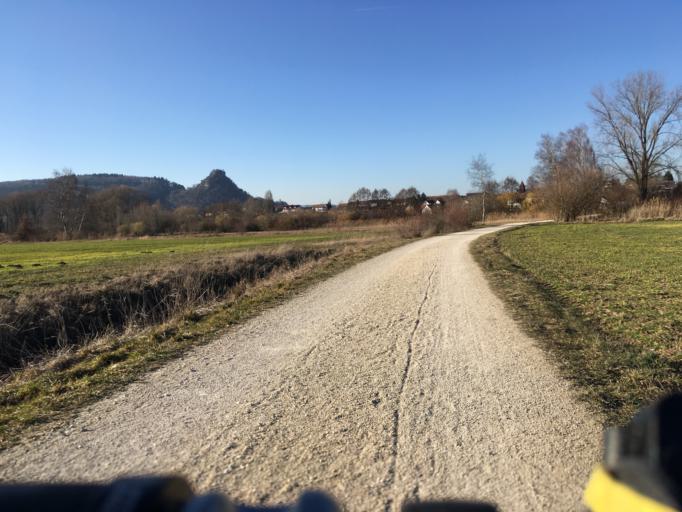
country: DE
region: Baden-Wuerttemberg
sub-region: Freiburg Region
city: Singen
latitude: 47.7876
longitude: 8.8447
